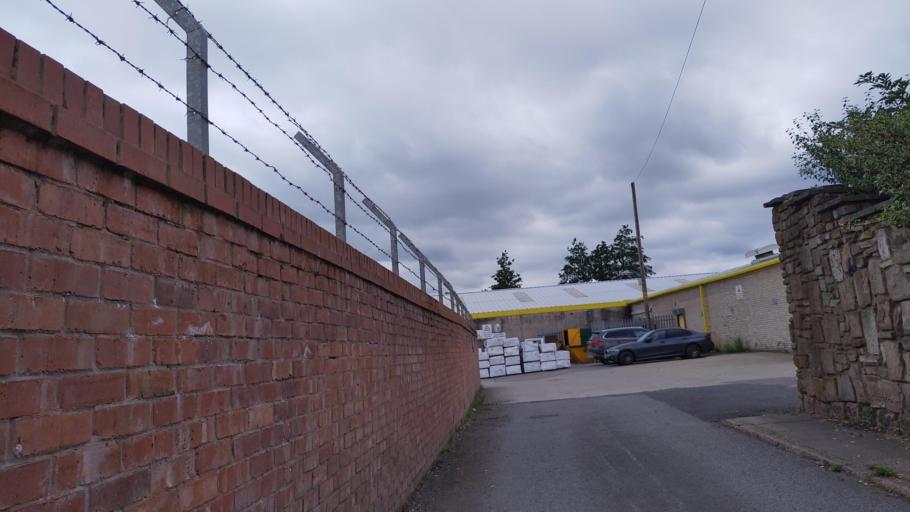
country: GB
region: England
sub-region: Lancashire
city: Adlington
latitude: 53.6123
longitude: -2.6025
